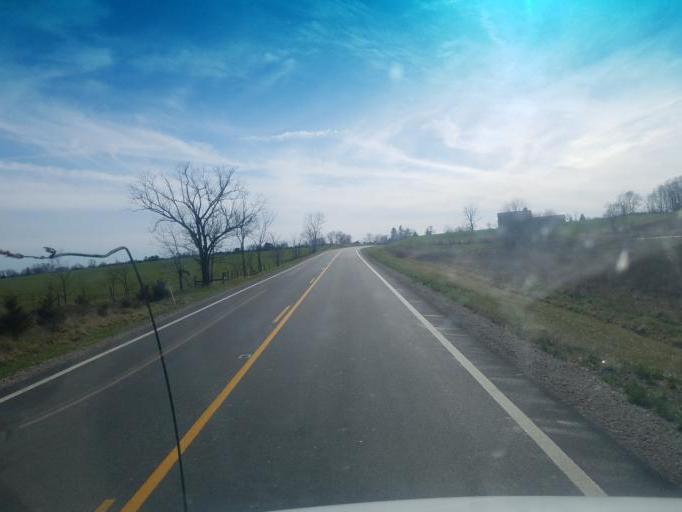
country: US
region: Ohio
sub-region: Union County
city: Marysville
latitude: 40.3325
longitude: -83.4543
